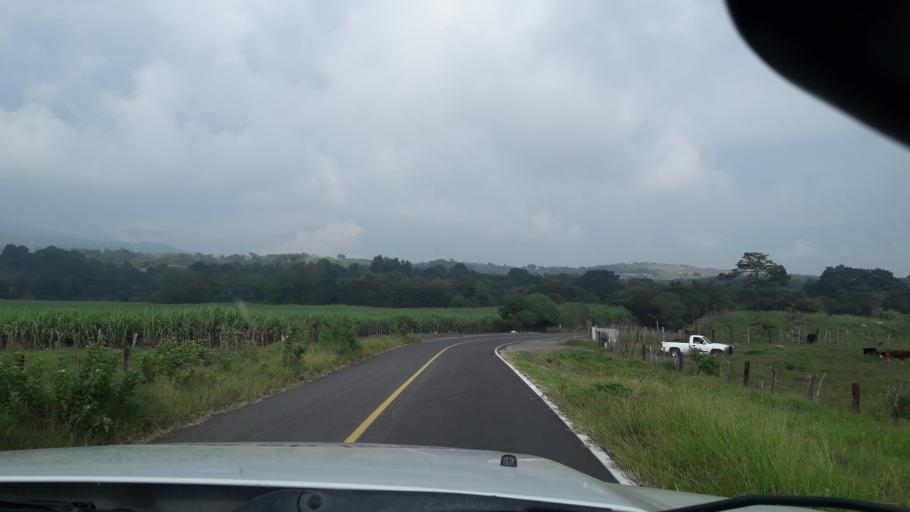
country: MX
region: Colima
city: Queseria
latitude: 19.4094
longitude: -103.6305
